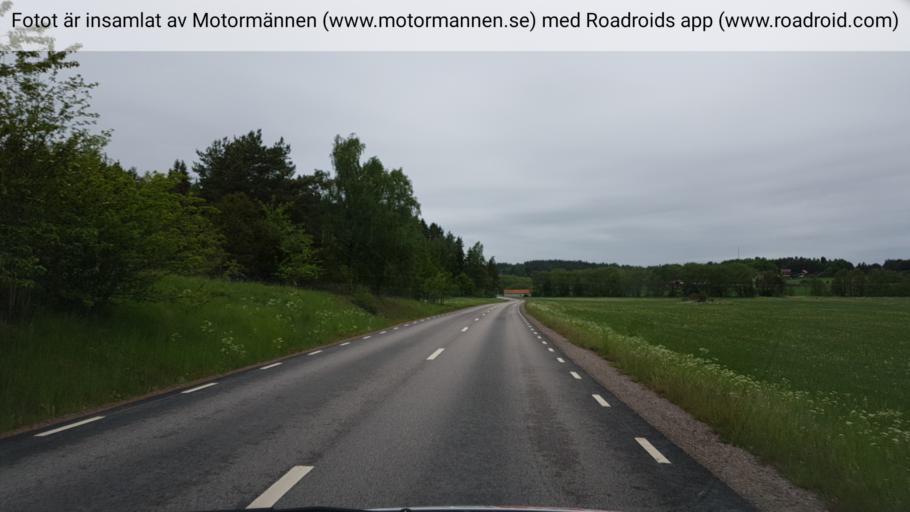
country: SE
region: Kalmar
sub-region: Vasterviks Kommun
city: Forserum
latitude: 57.9462
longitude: 16.4481
